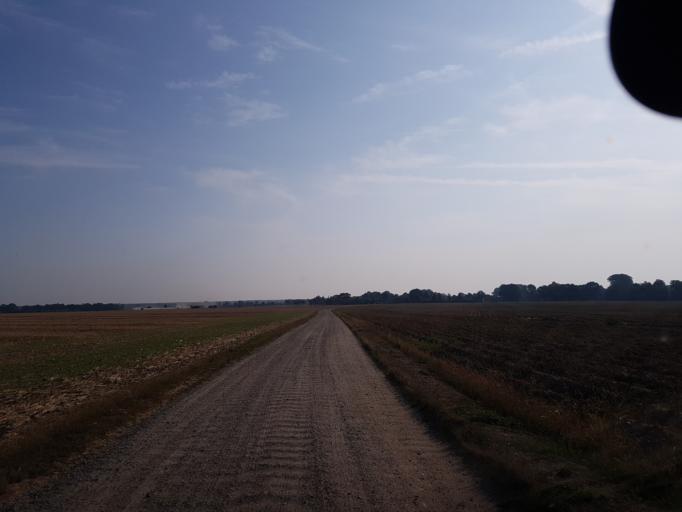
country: DE
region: Brandenburg
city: Finsterwalde
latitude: 51.6708
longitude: 13.6940
